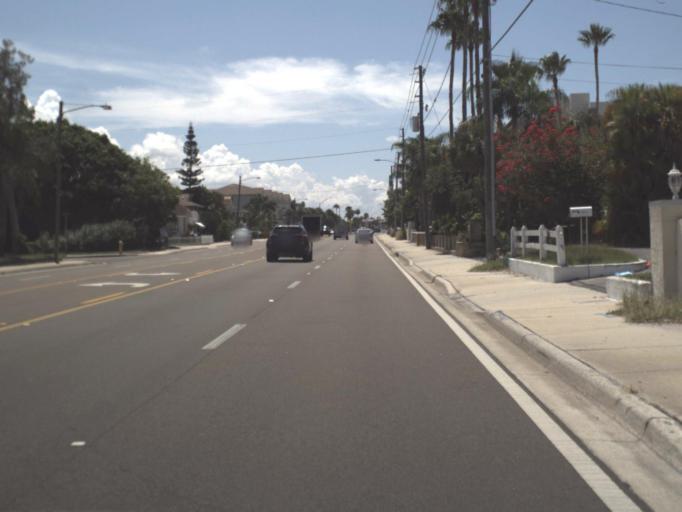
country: US
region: Florida
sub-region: Pinellas County
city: Redington Beach
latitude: 27.8064
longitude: -82.8084
